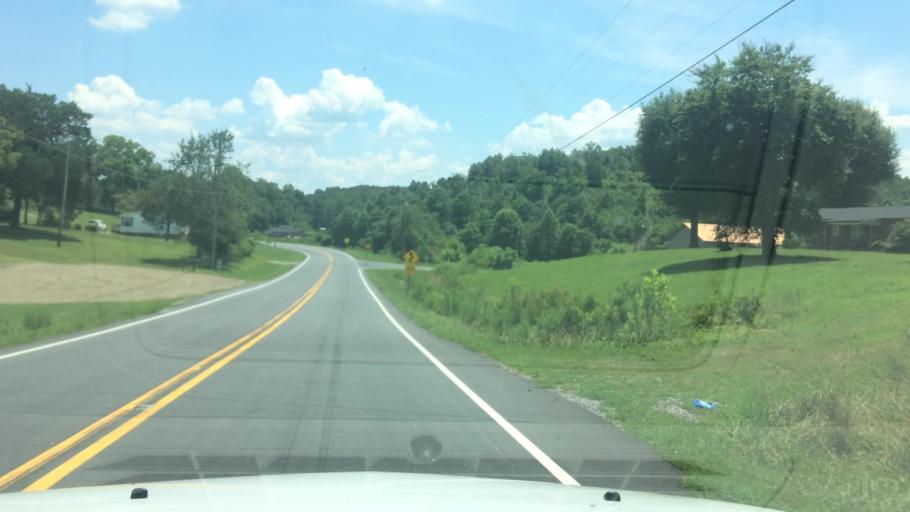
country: US
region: North Carolina
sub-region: Alexander County
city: Taylorsville
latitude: 35.9200
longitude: -81.2561
